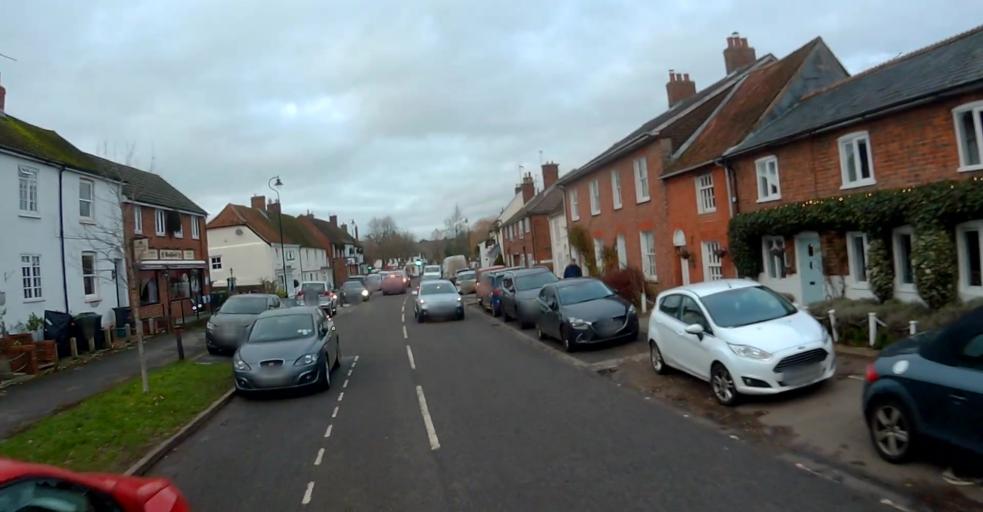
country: GB
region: England
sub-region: Hampshire
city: Overton
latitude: 51.2427
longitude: -1.2629
